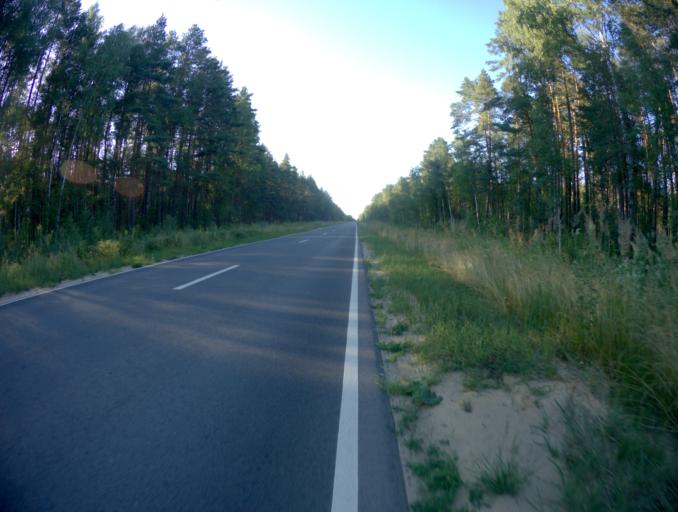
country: RU
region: Vladimir
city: Galitsy
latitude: 56.0854
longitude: 42.8685
